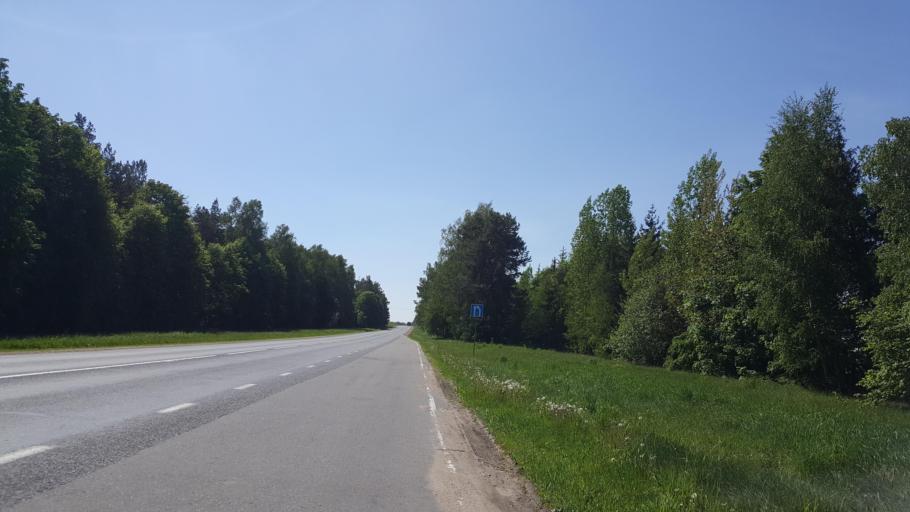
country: BY
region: Brest
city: Kamyanyets
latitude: 52.3536
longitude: 23.7762
